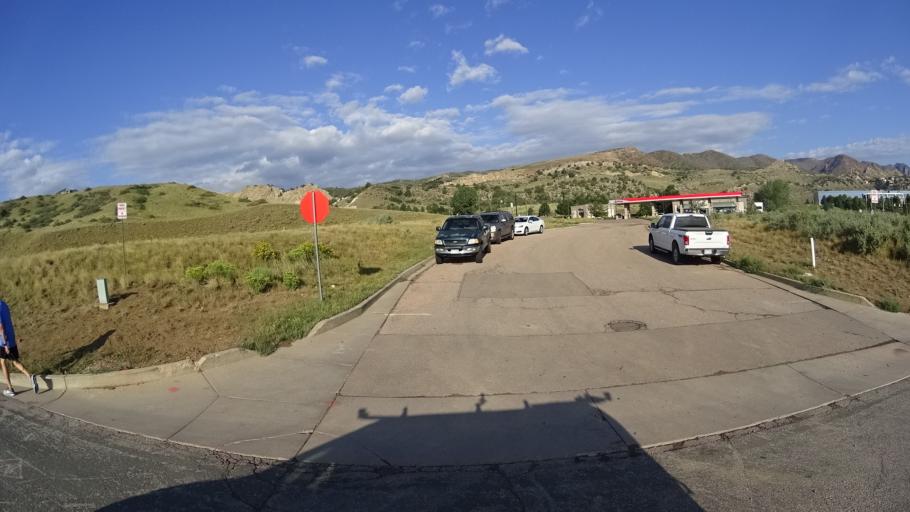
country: US
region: Colorado
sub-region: El Paso County
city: Manitou Springs
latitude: 38.8964
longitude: -104.8713
